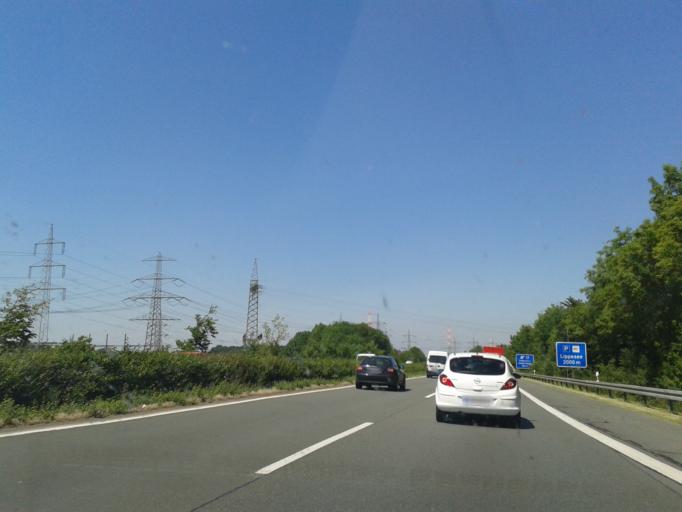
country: DE
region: North Rhine-Westphalia
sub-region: Regierungsbezirk Detmold
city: Paderborn
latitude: 51.7351
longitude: 8.7050
